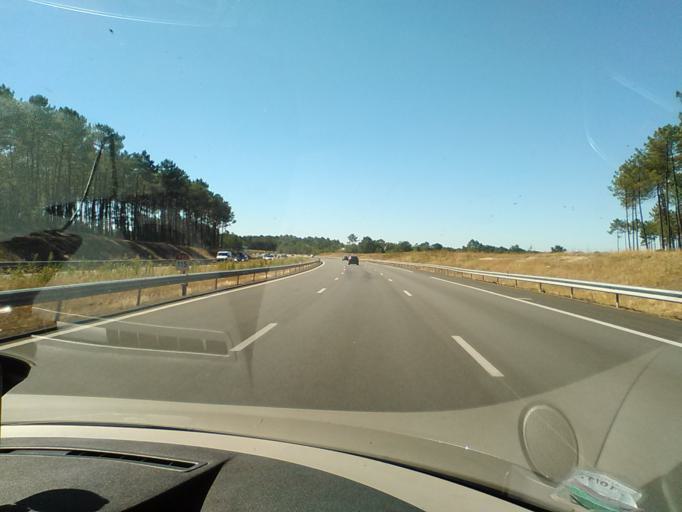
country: FR
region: Aquitaine
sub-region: Departement des Landes
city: Castets
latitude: 43.8934
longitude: -1.1344
